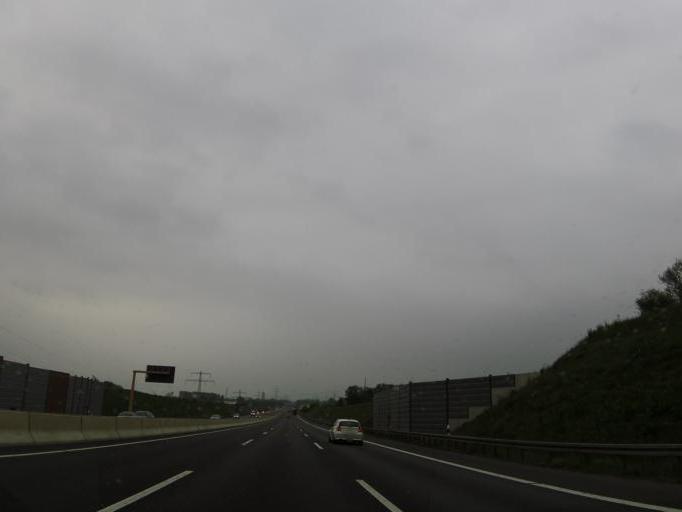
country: DE
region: Lower Saxony
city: Rosdorf
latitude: 51.5428
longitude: 9.8791
